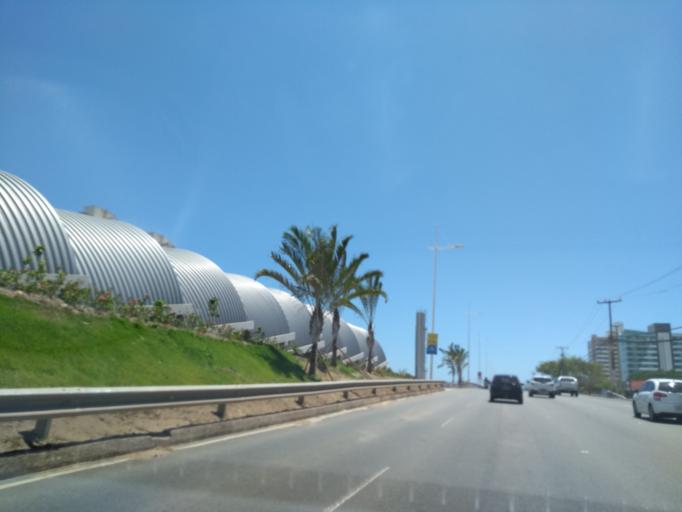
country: BR
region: Bahia
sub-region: Lauro De Freitas
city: Lauro de Freitas
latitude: -12.9384
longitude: -38.4063
